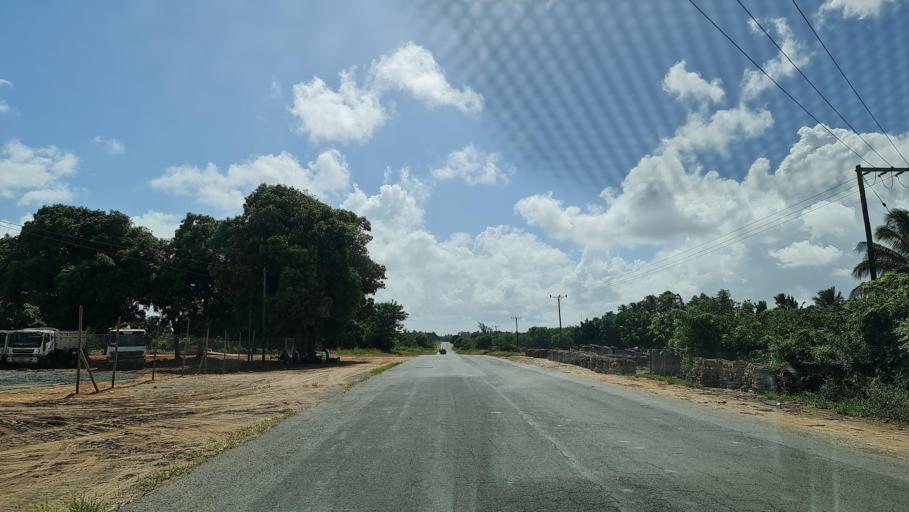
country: MZ
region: Gaza
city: Manjacaze
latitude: -24.6772
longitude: 34.5621
